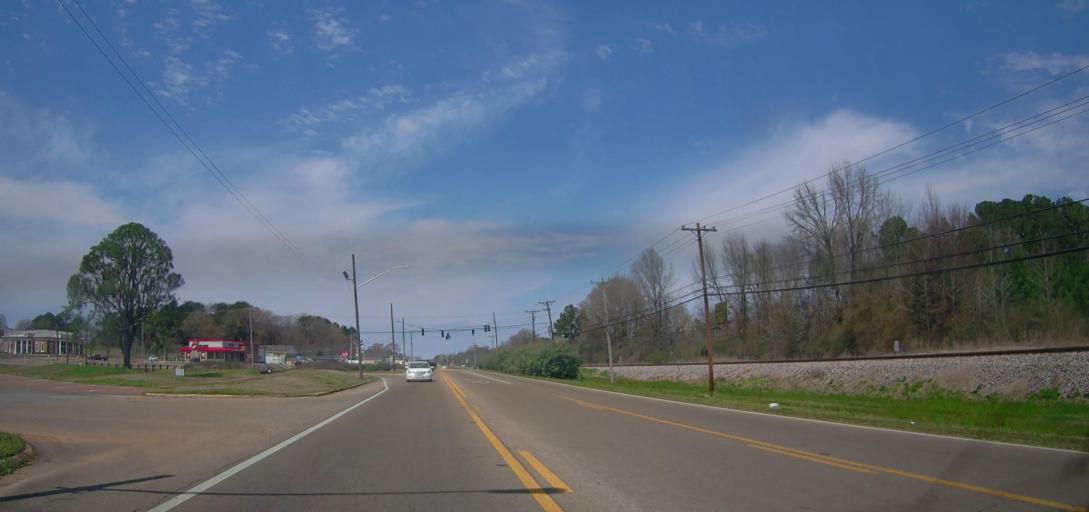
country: US
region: Mississippi
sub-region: Union County
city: New Albany
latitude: 34.4992
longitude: -89.0240
